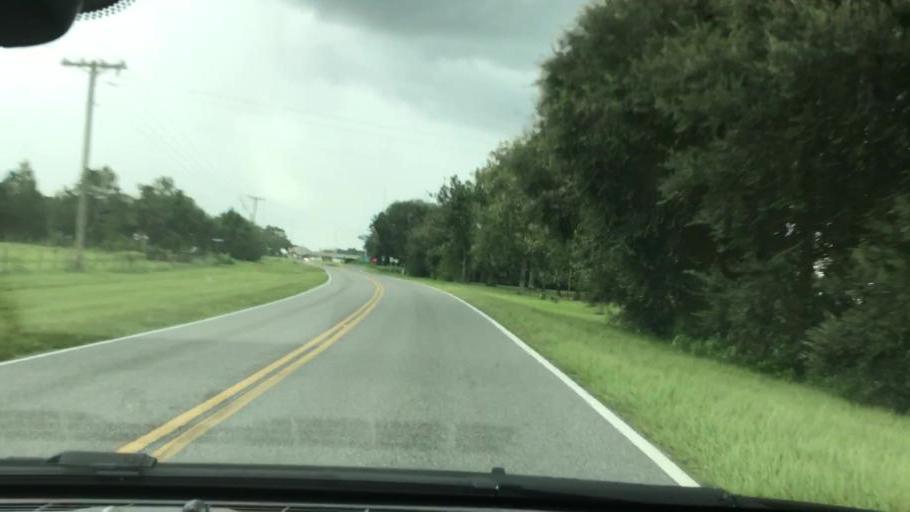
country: US
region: Florida
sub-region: Madison County
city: Madison
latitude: 30.3852
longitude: -83.3003
